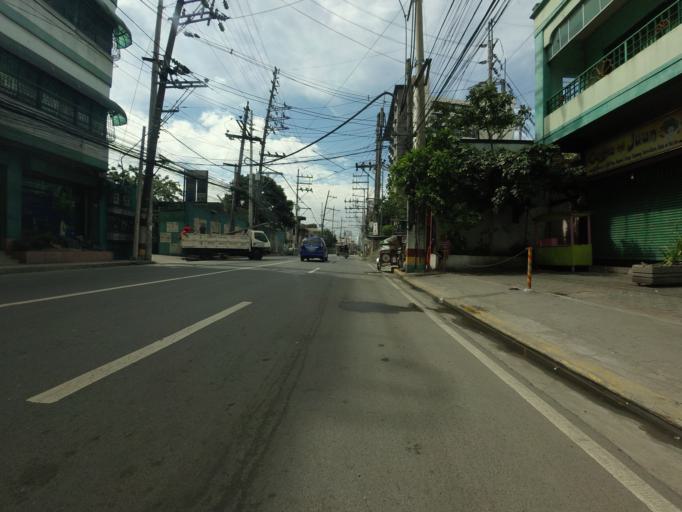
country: PH
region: Metro Manila
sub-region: San Juan
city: San Juan
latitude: 14.5805
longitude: 121.0092
